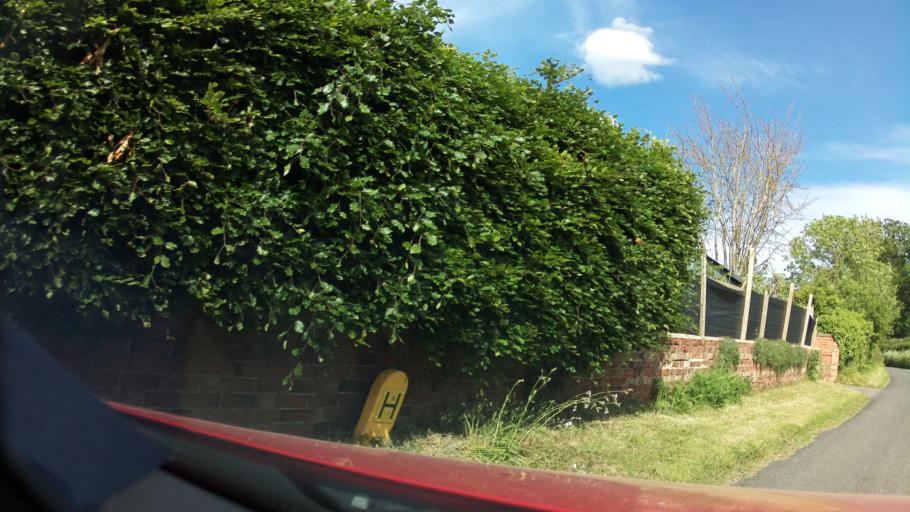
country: GB
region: England
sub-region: Gloucestershire
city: Chipping Campden
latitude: 52.0614
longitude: -1.8124
